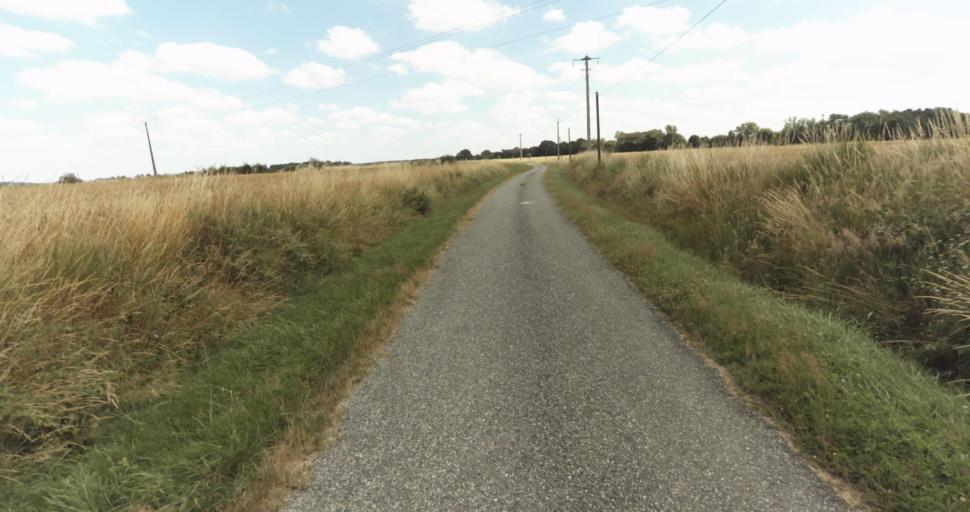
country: FR
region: Midi-Pyrenees
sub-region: Departement de la Haute-Garonne
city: Fontenilles
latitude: 43.5663
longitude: 1.1714
